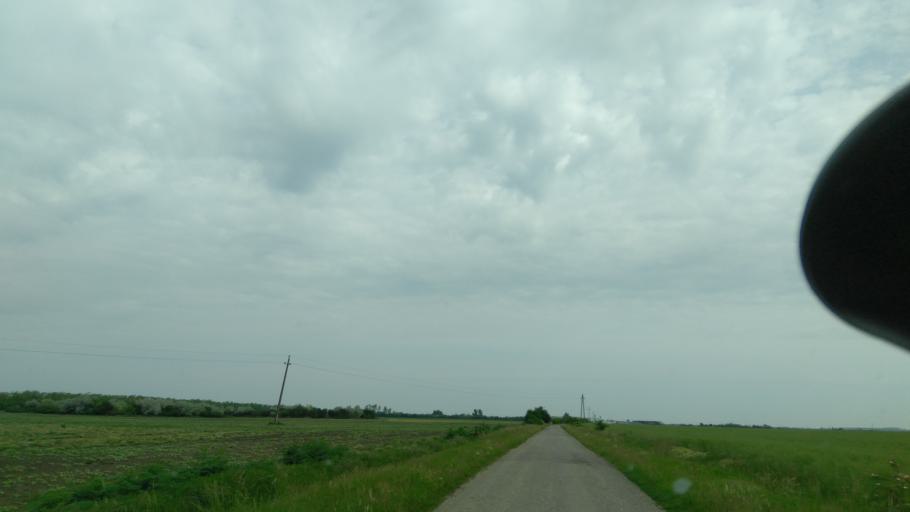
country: HU
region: Bekes
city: Szeghalom
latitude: 47.0397
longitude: 21.1544
